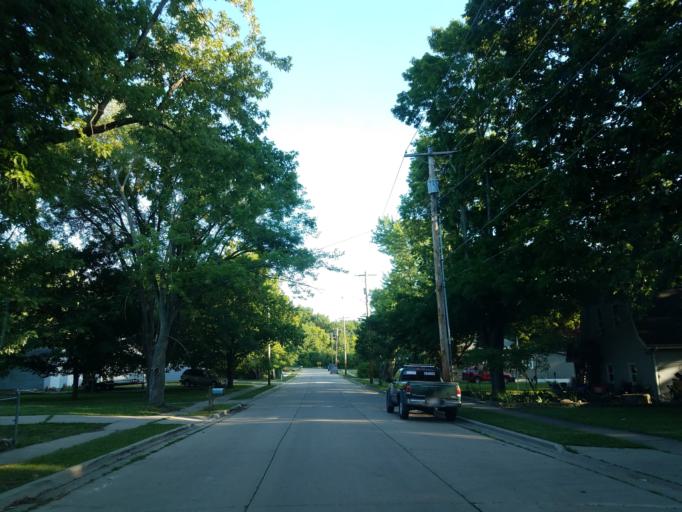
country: US
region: Illinois
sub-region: McLean County
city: Bloomington
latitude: 40.4660
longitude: -89.0120
